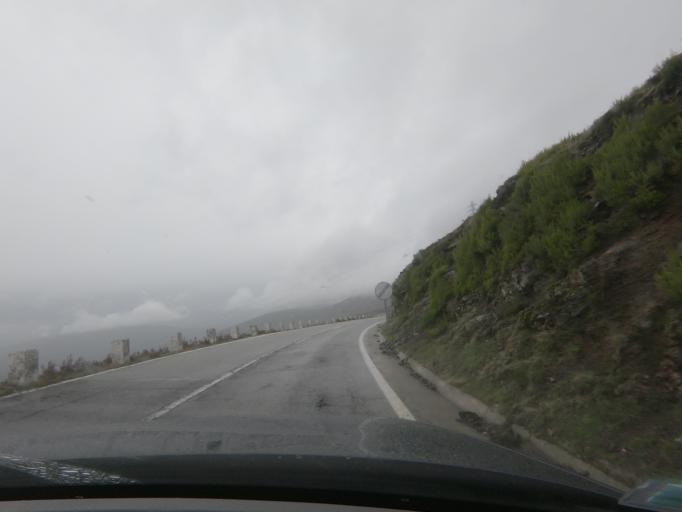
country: PT
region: Vila Real
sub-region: Mondim de Basto
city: Mondim de Basto
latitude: 41.3238
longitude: -7.8860
